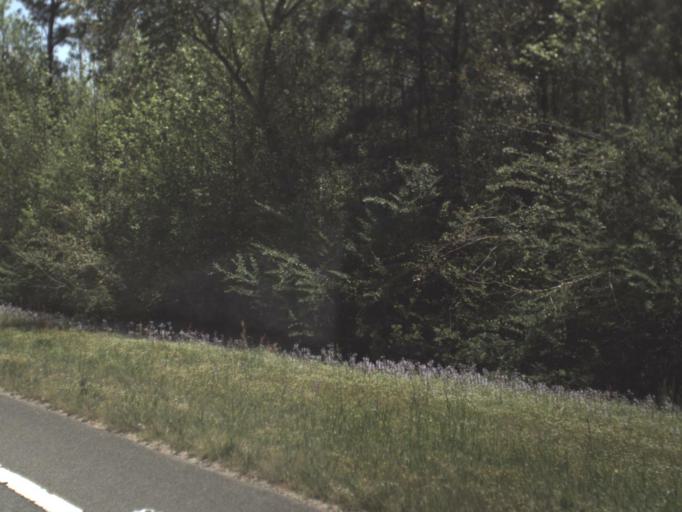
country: US
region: Florida
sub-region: Escambia County
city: Century
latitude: 30.9726
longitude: -87.2414
